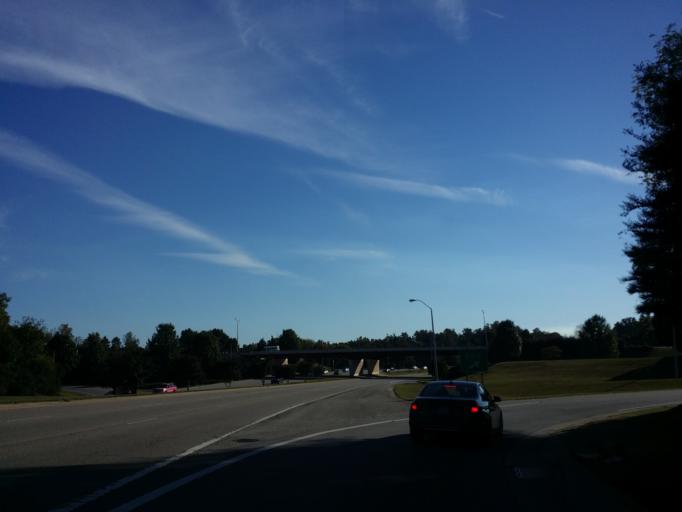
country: US
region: North Carolina
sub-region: Wake County
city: Raleigh
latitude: 35.7712
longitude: -78.6442
